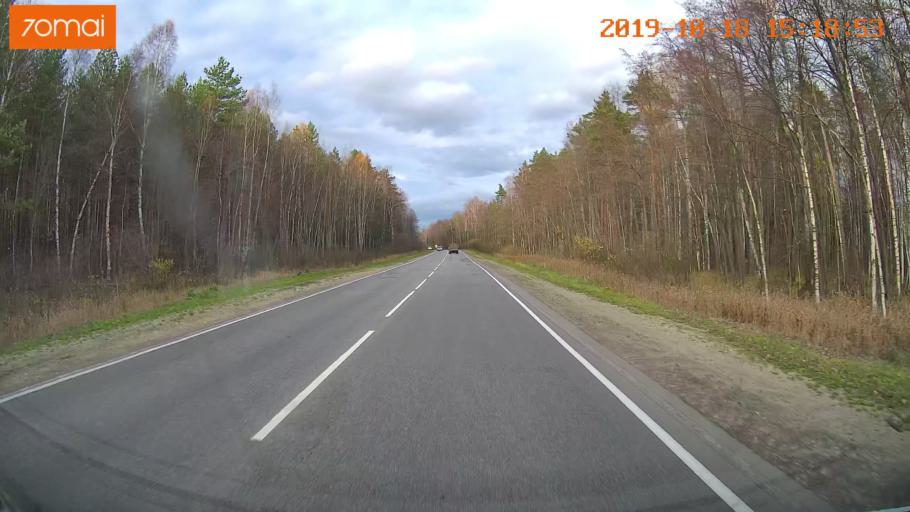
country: RU
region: Vladimir
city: Anopino
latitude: 55.6651
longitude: 40.7332
